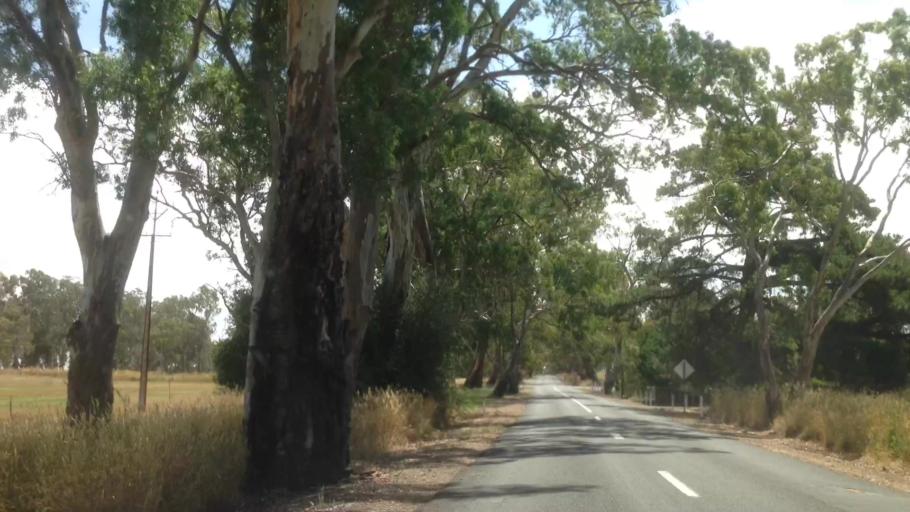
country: AU
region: South Australia
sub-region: Adelaide Hills
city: Birdwood
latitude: -34.7907
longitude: 138.9563
